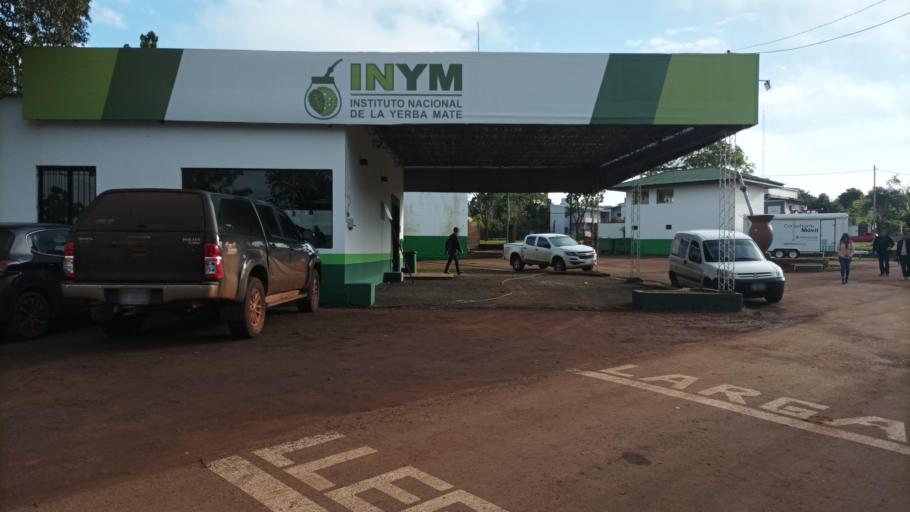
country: AR
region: Misiones
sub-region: Departamento de Apostoles
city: Apostoles
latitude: -27.9112
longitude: -55.7593
